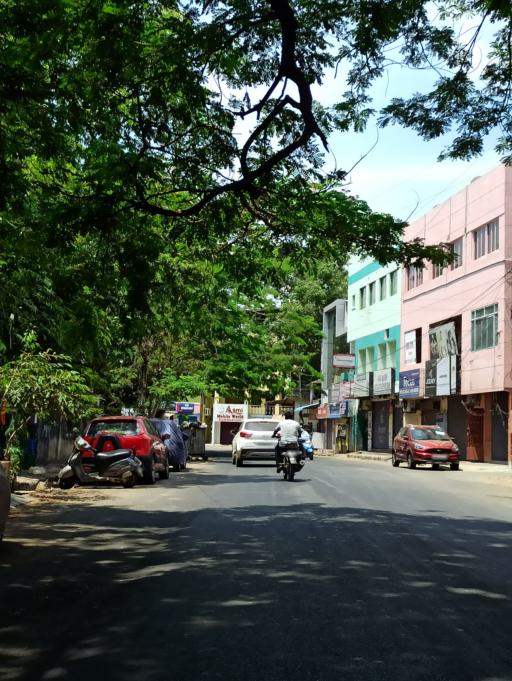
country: IN
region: Tamil Nadu
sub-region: Chennai
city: Chetput
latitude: 13.0790
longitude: 80.2374
